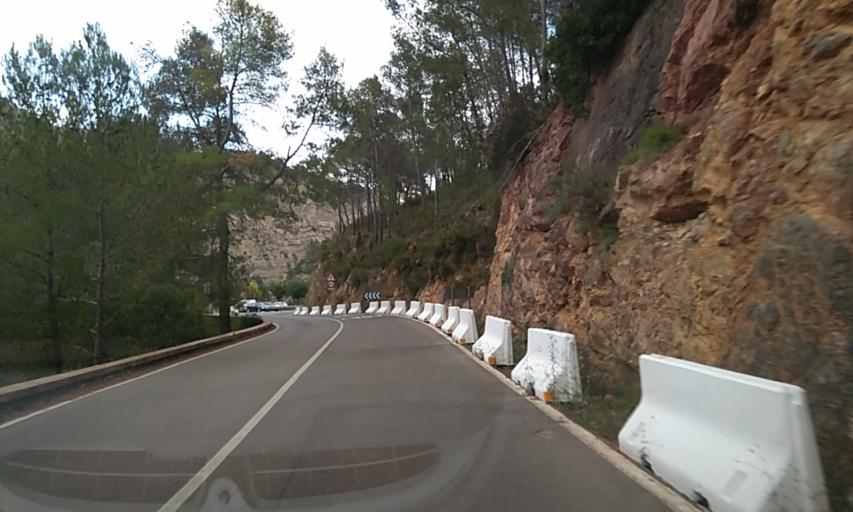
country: ES
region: Valencia
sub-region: Provincia de Castello
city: Montanejos
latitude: 40.0745
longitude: -0.5319
